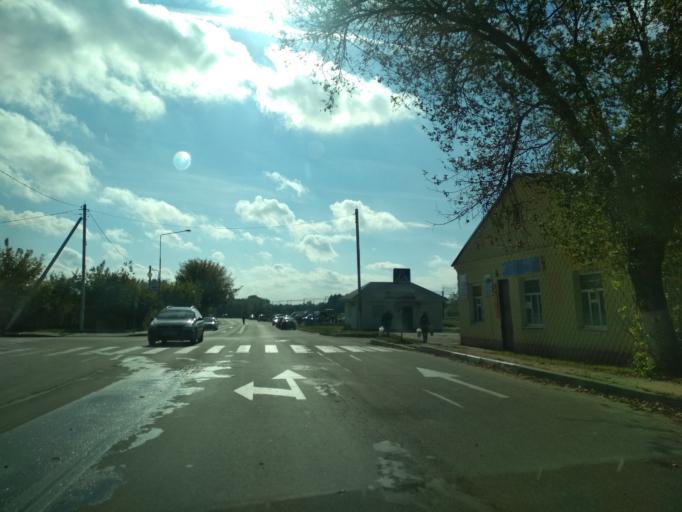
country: BY
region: Minsk
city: Mar''ina Horka
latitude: 53.5061
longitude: 28.1462
